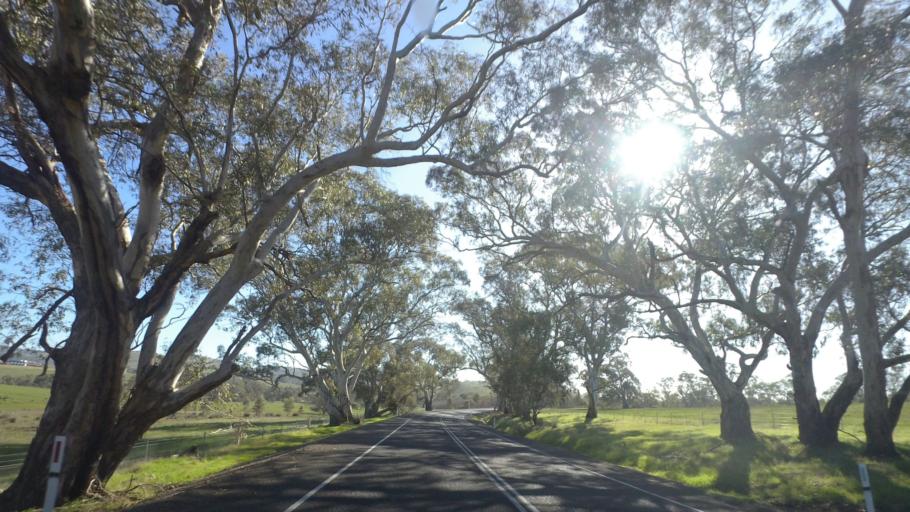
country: AU
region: Victoria
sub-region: Mount Alexander
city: Castlemaine
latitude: -36.9508
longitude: 144.3401
